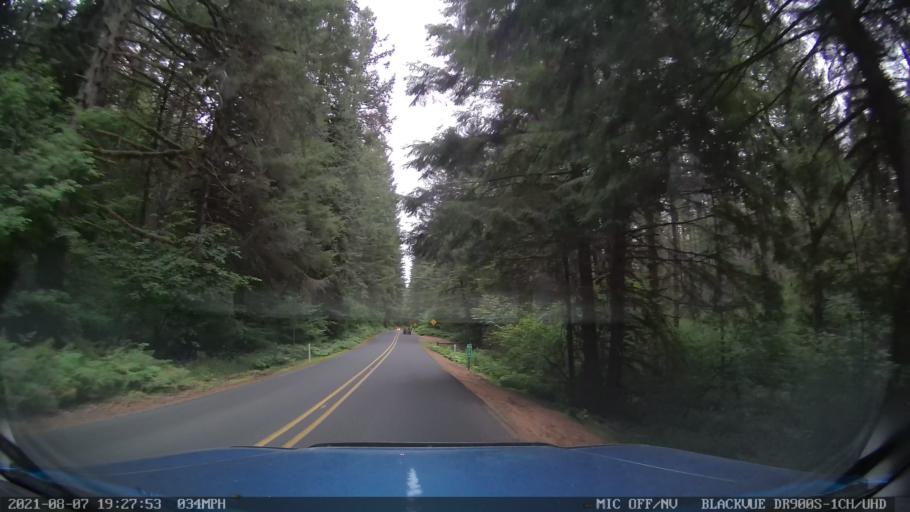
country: US
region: Oregon
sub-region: Linn County
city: Lyons
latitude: 44.8798
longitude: -122.6415
